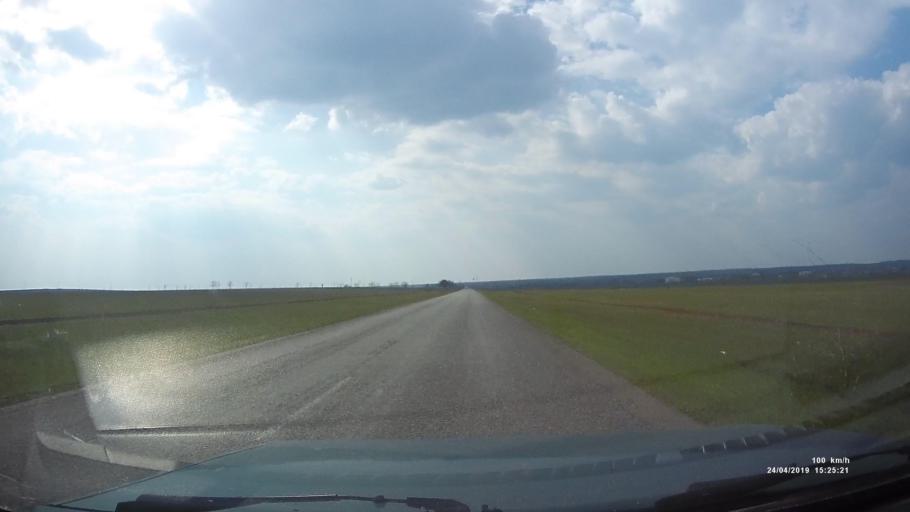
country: RU
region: Rostov
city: Remontnoye
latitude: 46.5520
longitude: 43.0495
